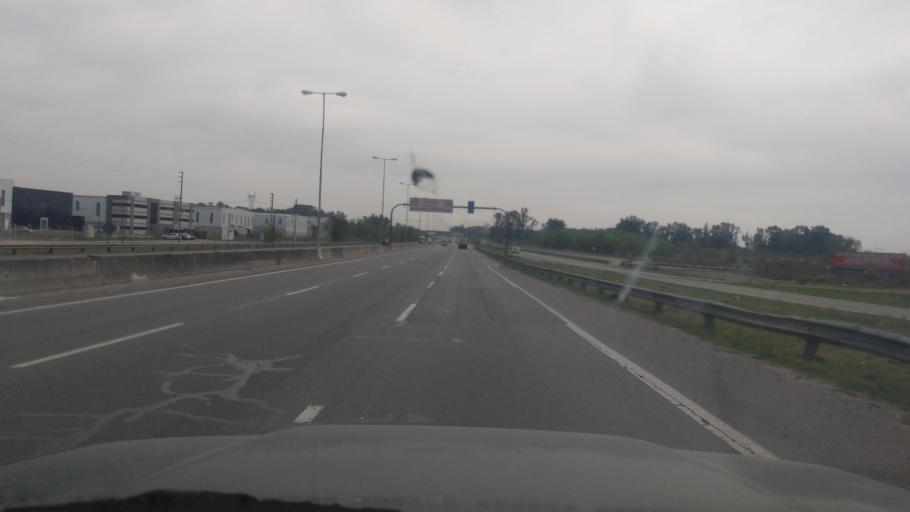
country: AR
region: Buenos Aires
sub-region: Partido de Pilar
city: Pilar
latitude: -34.4104
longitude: -59.0058
